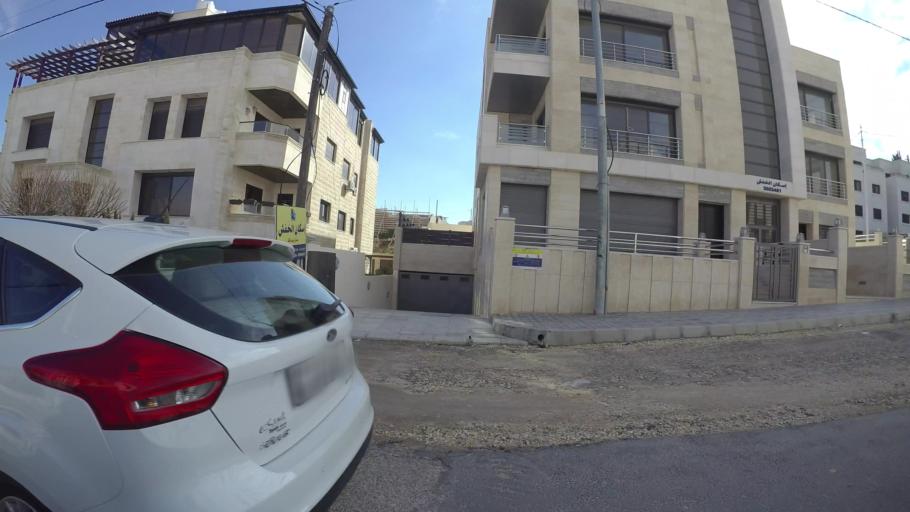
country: JO
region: Amman
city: Al Jubayhah
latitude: 32.0076
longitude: 35.8426
